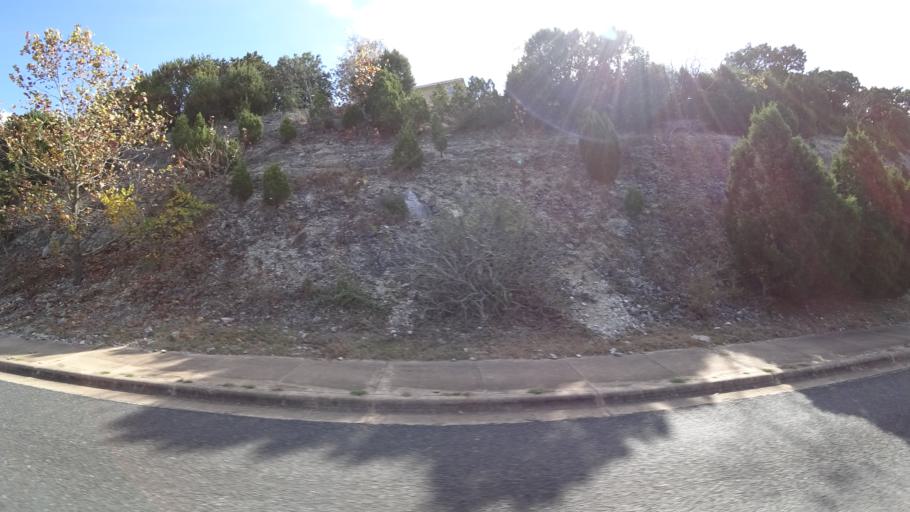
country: US
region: Texas
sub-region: Williamson County
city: Jollyville
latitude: 30.4231
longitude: -97.7912
